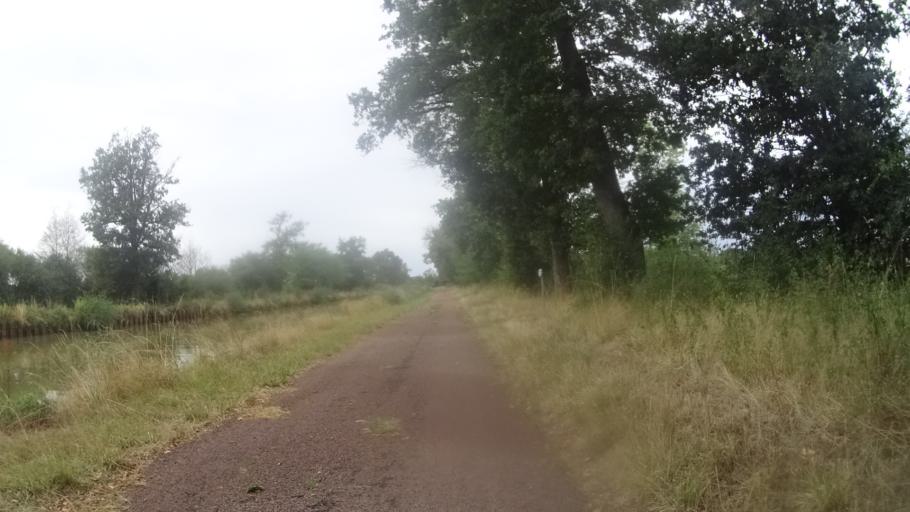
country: FR
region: Bourgogne
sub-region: Departement de la Nievre
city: Imphy
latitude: 46.8545
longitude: 3.2949
